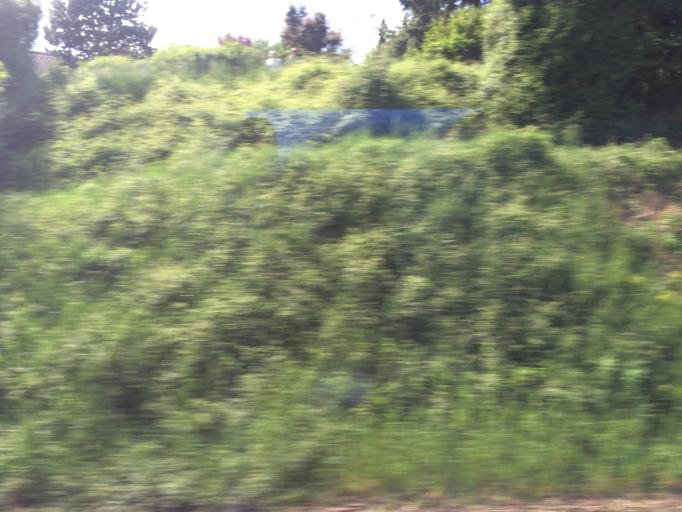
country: DE
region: Bavaria
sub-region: Regierungsbezirk Unterfranken
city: Kitzingen
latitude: 49.7422
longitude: 10.1580
